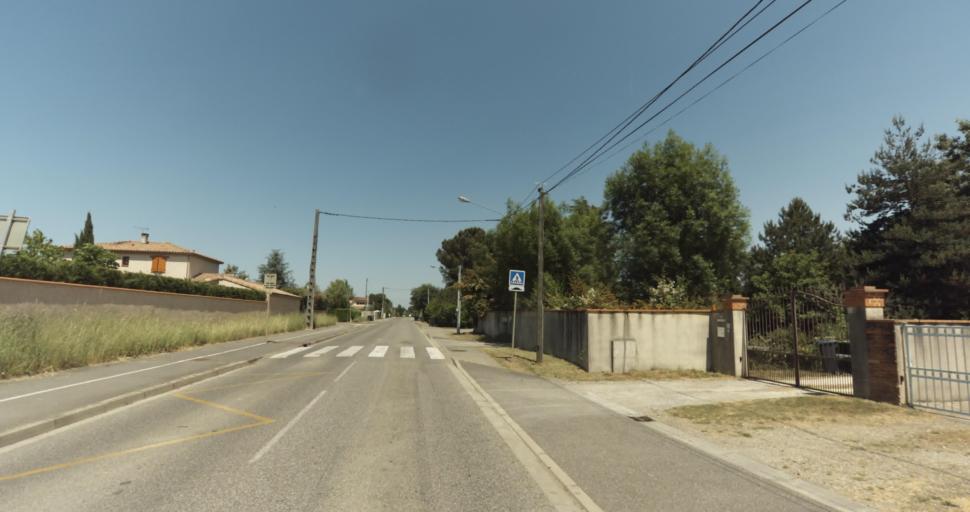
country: FR
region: Midi-Pyrenees
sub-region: Departement de la Haute-Garonne
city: Leguevin
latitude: 43.5906
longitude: 1.2281
